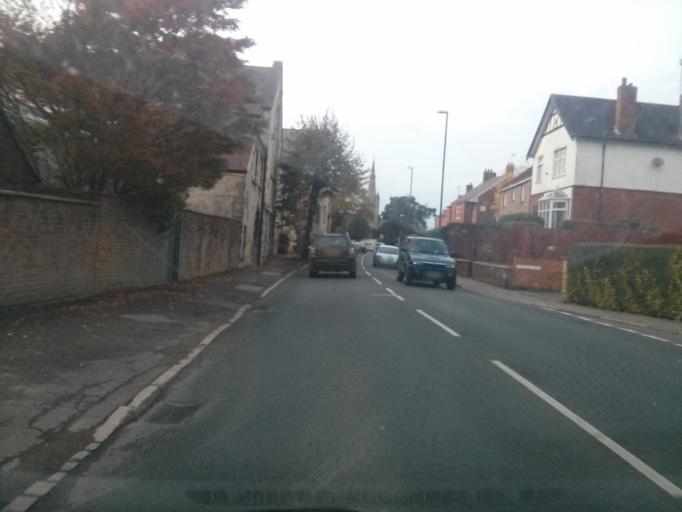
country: GB
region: England
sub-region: Gloucestershire
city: Stonehouse
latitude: 51.7432
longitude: -2.2783
